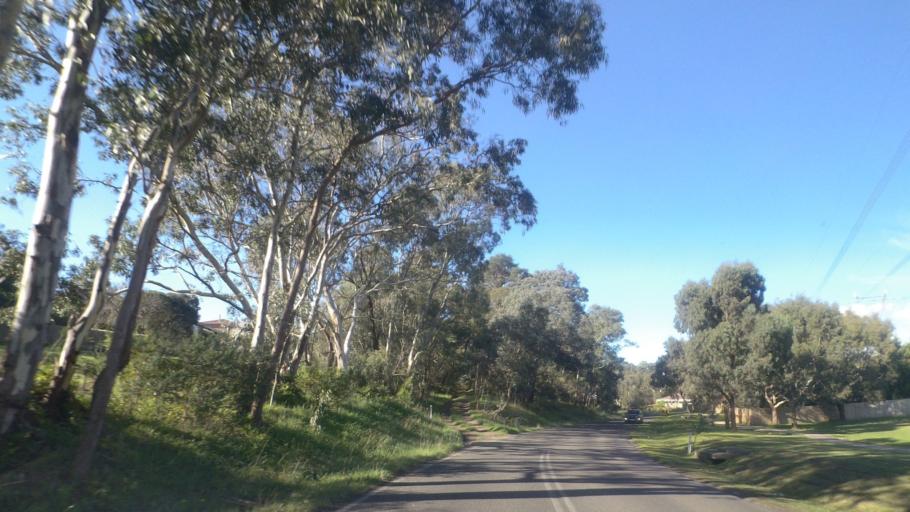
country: AU
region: Victoria
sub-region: Nillumbik
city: Eltham North
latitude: -37.6876
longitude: 145.1495
